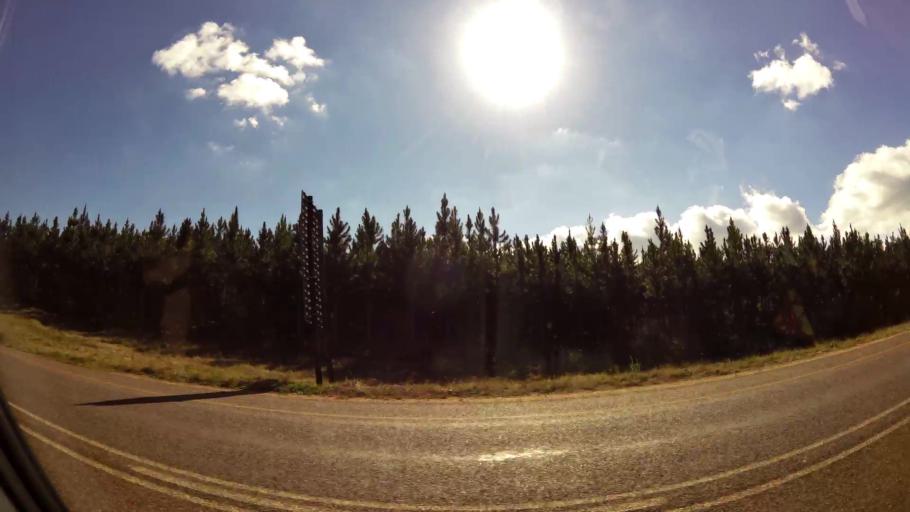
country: ZA
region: Limpopo
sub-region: Capricorn District Municipality
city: Mankoeng
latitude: -23.9080
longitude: 29.9833
